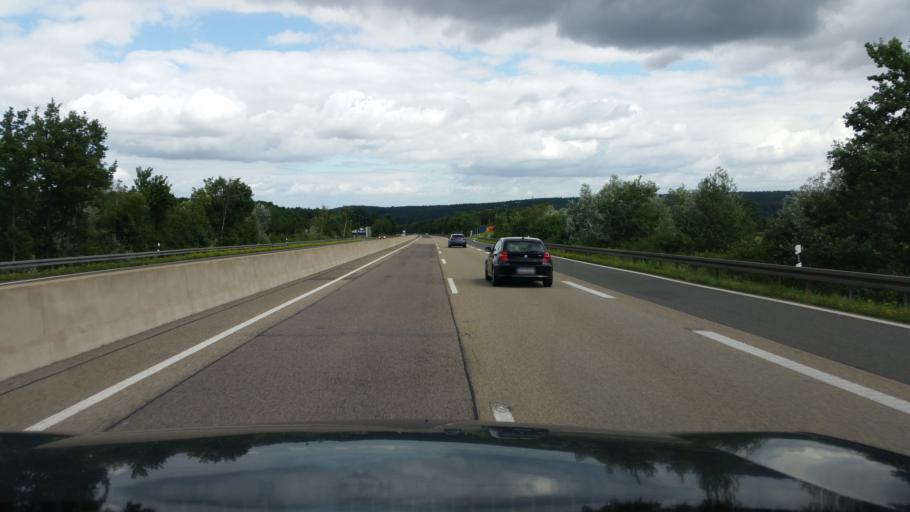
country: DE
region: North Rhine-Westphalia
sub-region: Regierungsbezirk Koln
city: Mechernich
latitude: 50.6048
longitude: 6.7082
